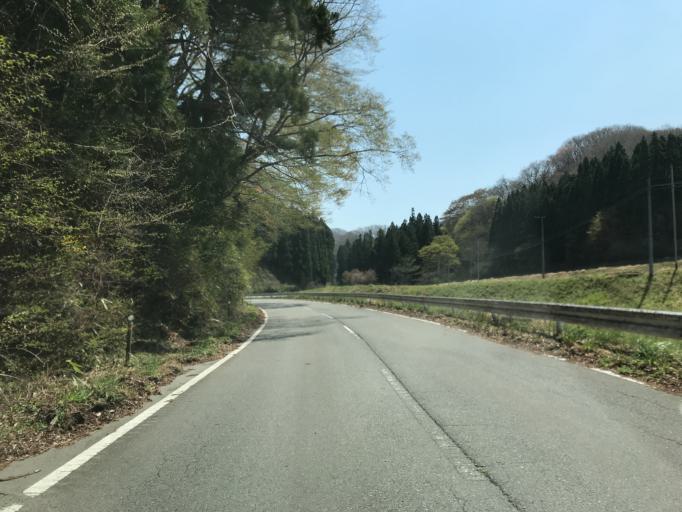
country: JP
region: Fukushima
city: Ishikawa
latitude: 36.9865
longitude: 140.6178
